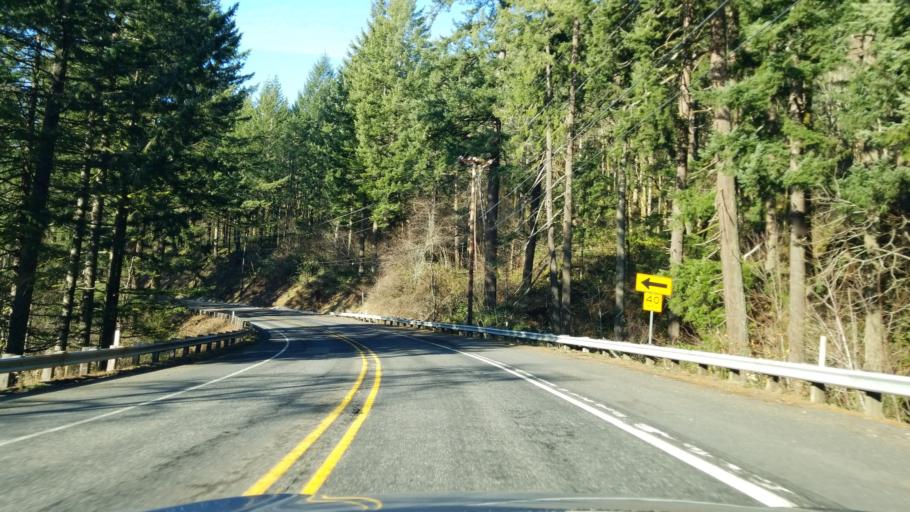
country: US
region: Washington
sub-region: Clark County
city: Washougal
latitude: 45.5979
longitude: -122.1245
